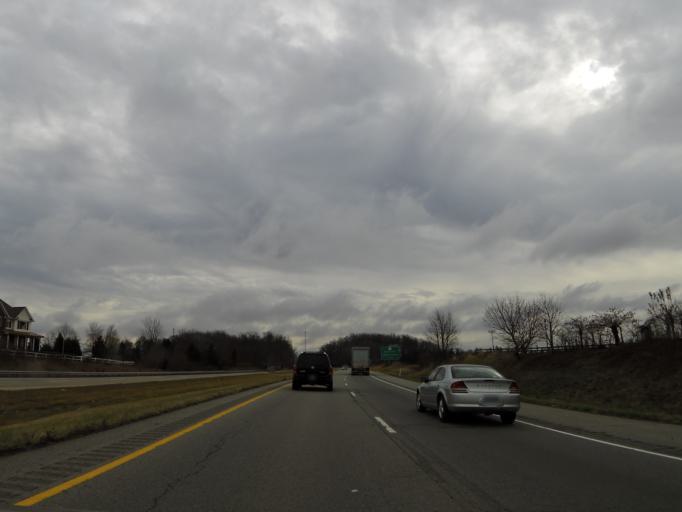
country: US
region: Indiana
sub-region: Ripley County
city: Sunman
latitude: 39.2848
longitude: -84.9726
